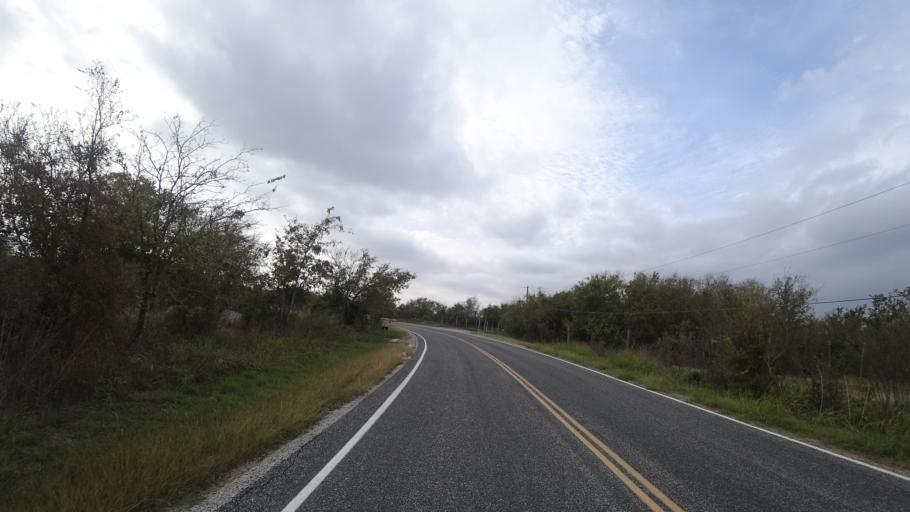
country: US
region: Texas
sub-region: Travis County
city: Manor
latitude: 30.3841
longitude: -97.5859
